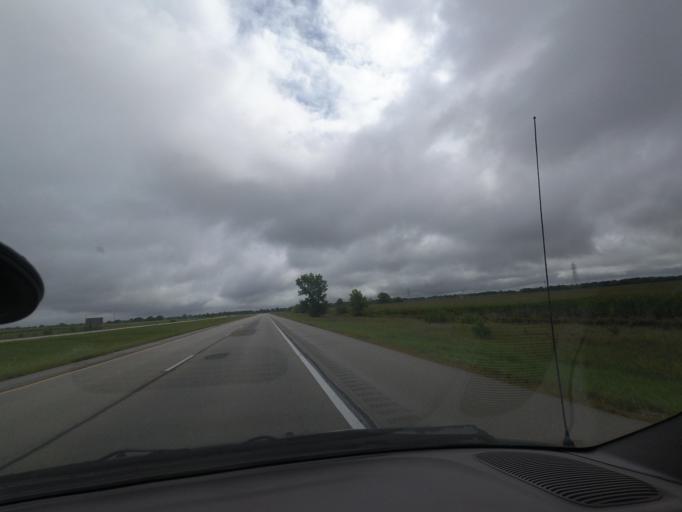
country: US
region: Illinois
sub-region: Piatt County
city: Monticello
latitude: 40.0310
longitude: -88.6131
